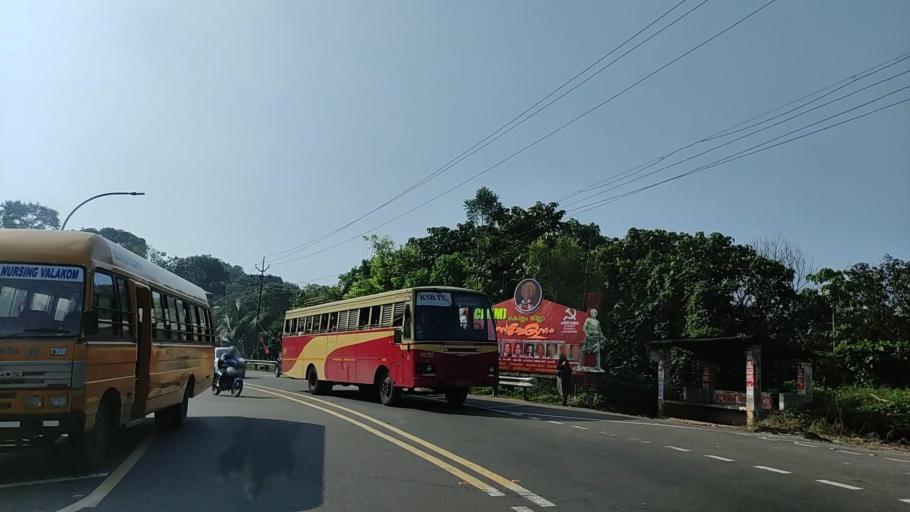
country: IN
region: Kerala
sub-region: Kollam
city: Punalur
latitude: 8.9639
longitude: 76.8341
